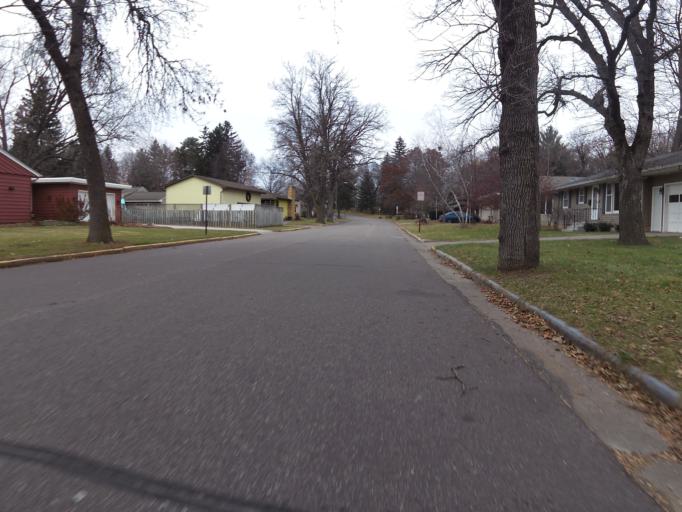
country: US
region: Wisconsin
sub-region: Pierce County
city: River Falls
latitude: 44.8533
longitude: -92.6147
